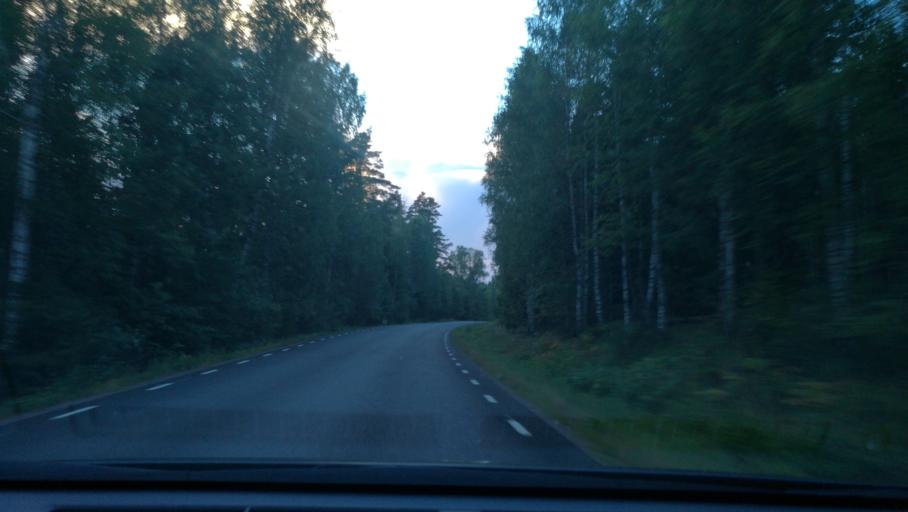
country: SE
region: OEstergoetland
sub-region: Norrkopings Kommun
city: Jursla
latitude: 58.8080
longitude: 16.1009
